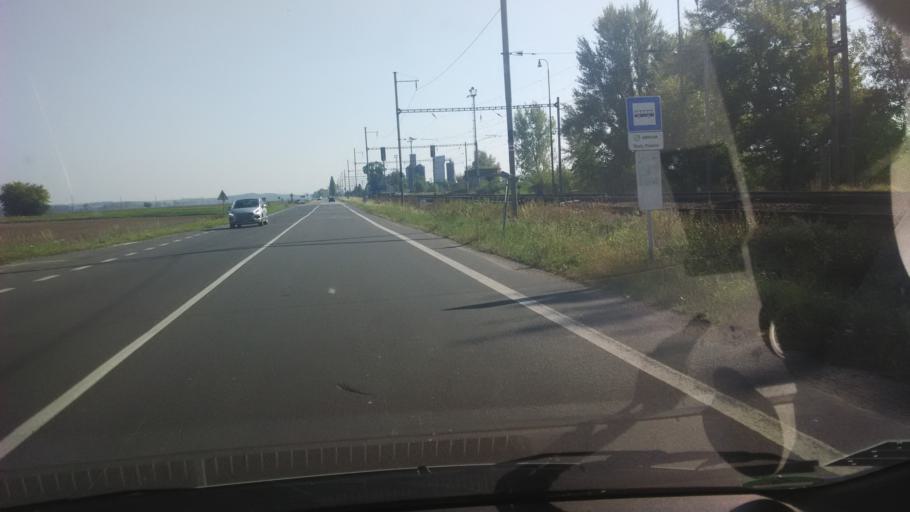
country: SK
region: Nitriansky
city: Tlmace
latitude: 48.2840
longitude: 18.5457
